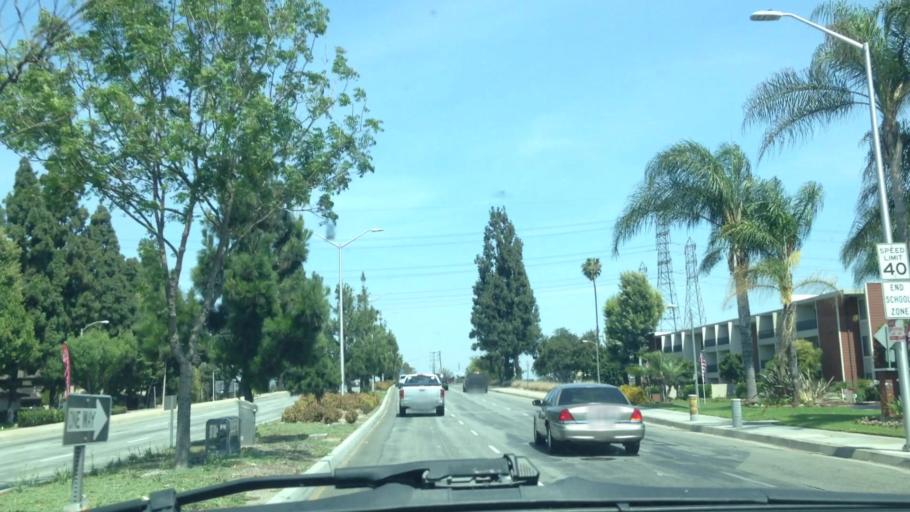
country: US
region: California
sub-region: Los Angeles County
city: Downey
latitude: 33.9172
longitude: -118.1144
